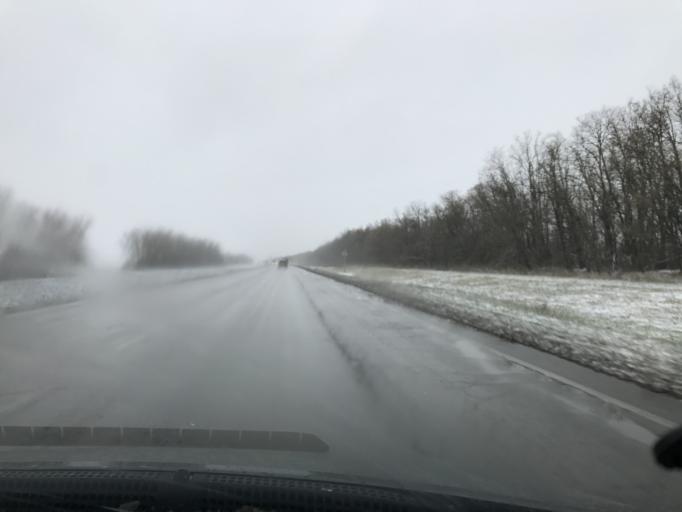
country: RU
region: Rostov
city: Yegorlykskaya
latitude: 46.6304
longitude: 40.5883
